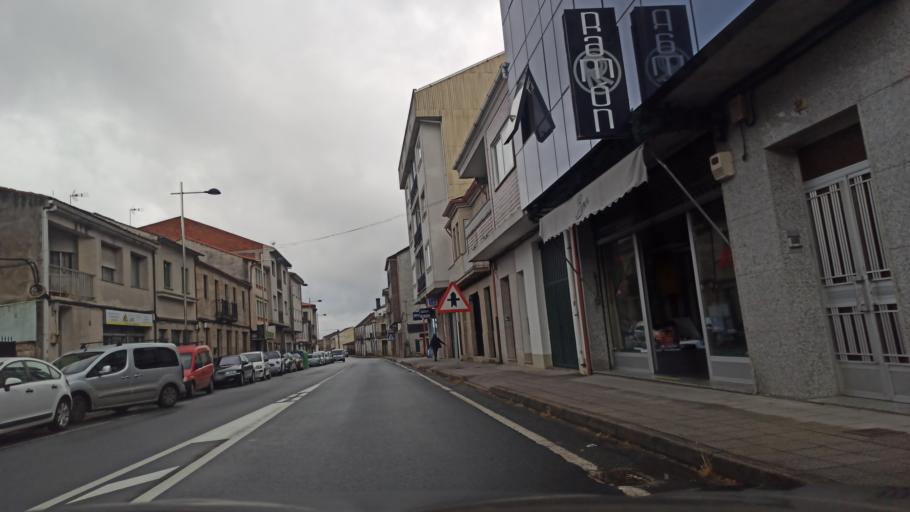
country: ES
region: Galicia
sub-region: Provincia da Coruna
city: Santiso
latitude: 42.7635
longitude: -8.0179
